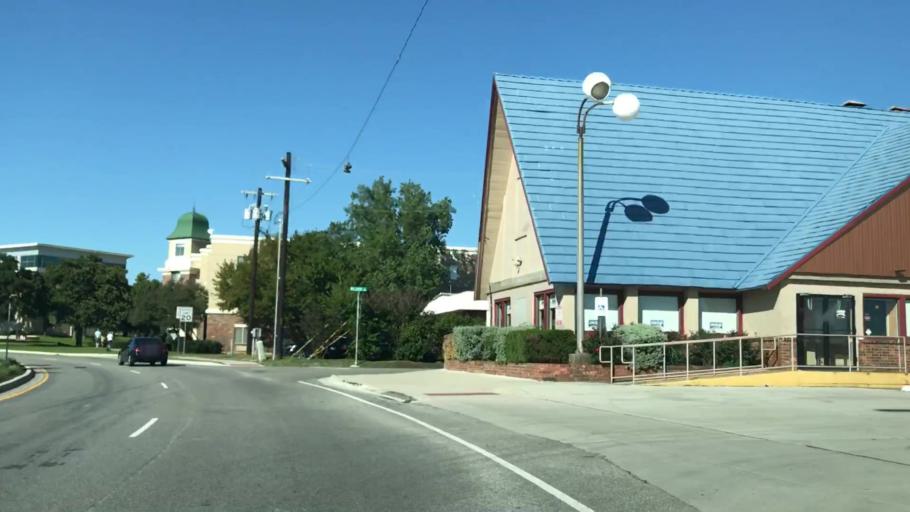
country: US
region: Texas
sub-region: Denton County
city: Denton
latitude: 33.2054
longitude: -97.1529
